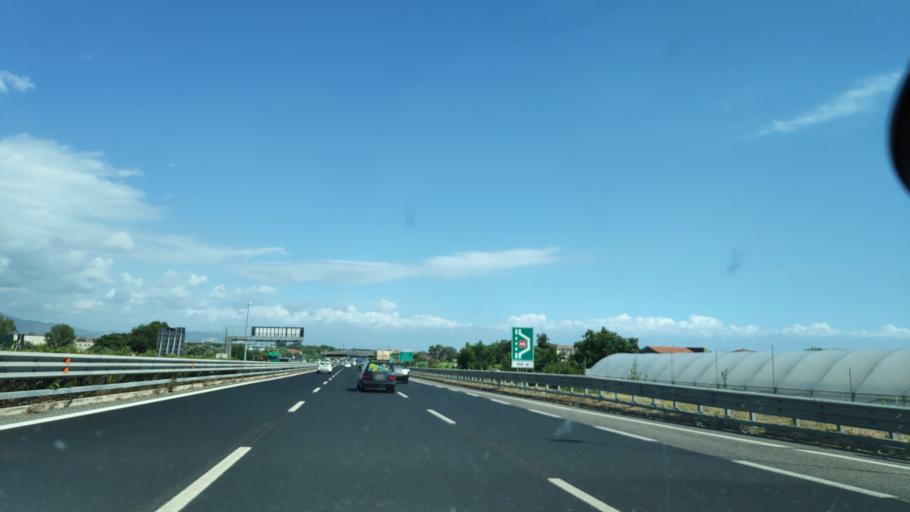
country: IT
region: Campania
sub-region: Provincia di Salerno
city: Pontecagnano
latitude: 40.6545
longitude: 14.8686
